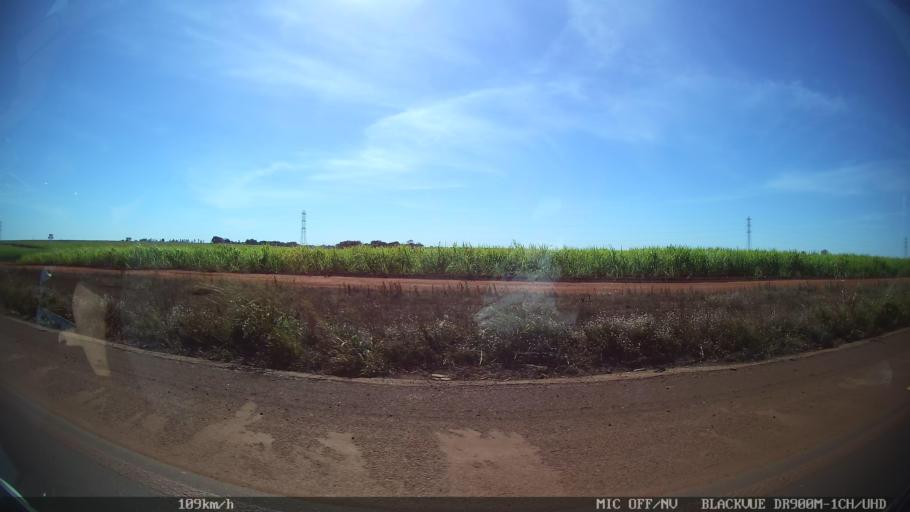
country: BR
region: Sao Paulo
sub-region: Guaira
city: Guaira
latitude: -20.4462
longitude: -48.4284
